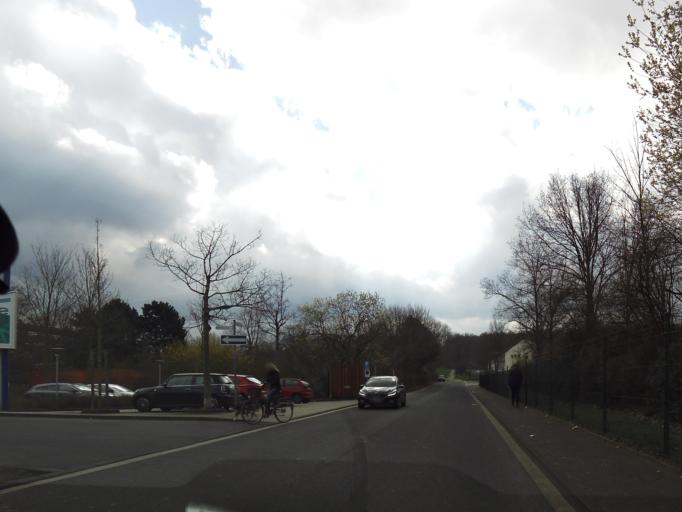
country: DE
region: North Rhine-Westphalia
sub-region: Regierungsbezirk Koln
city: Rheinbach
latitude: 50.6194
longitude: 6.9327
